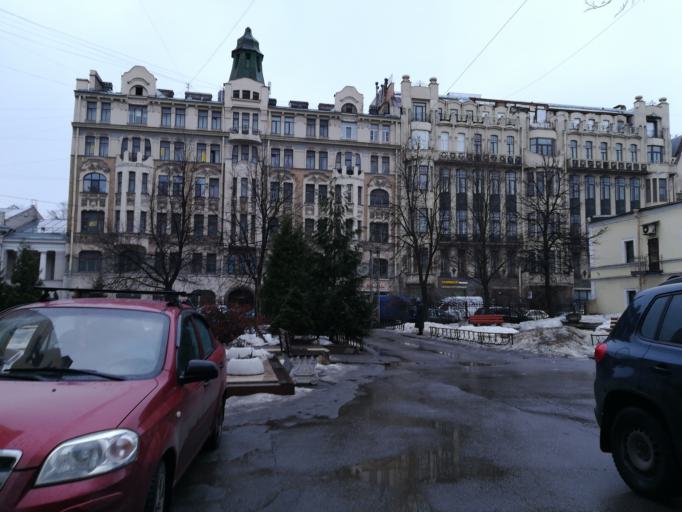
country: RU
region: St.-Petersburg
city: Petrogradka
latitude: 59.9571
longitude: 30.3307
